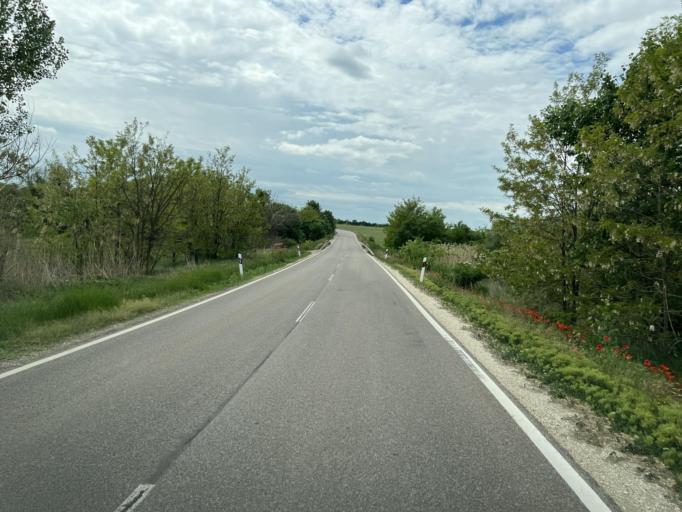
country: HU
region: Pest
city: Zsambok
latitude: 47.5239
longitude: 19.5991
